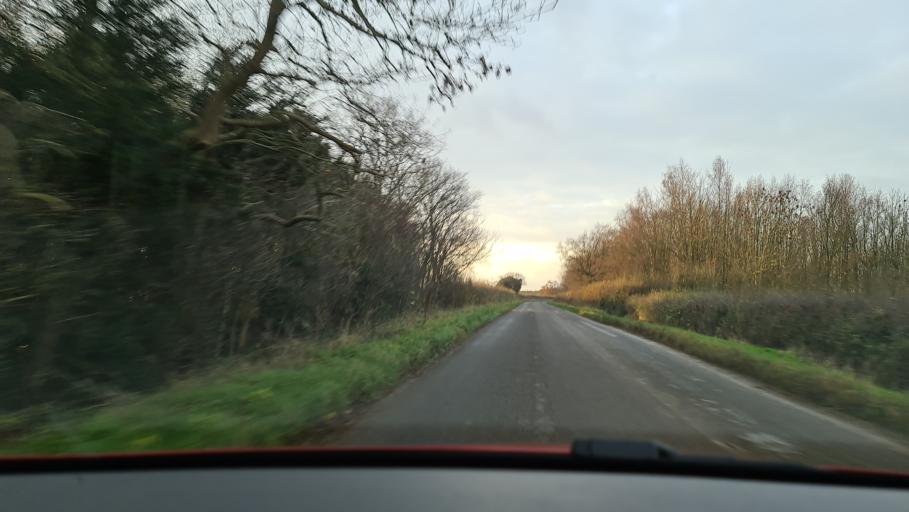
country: GB
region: England
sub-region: Oxfordshire
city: Somerton
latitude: 51.8898
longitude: -1.2733
